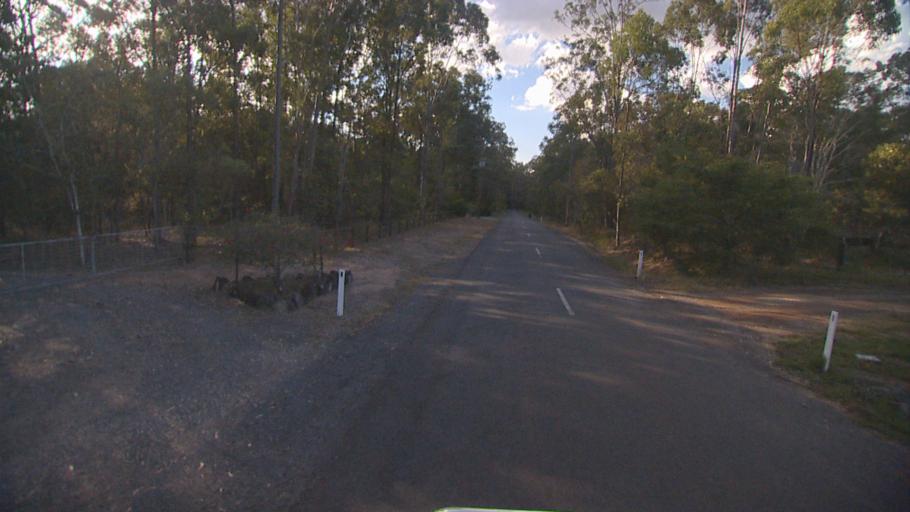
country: AU
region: Queensland
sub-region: Ipswich
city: Springfield Lakes
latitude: -27.6937
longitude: 152.9541
